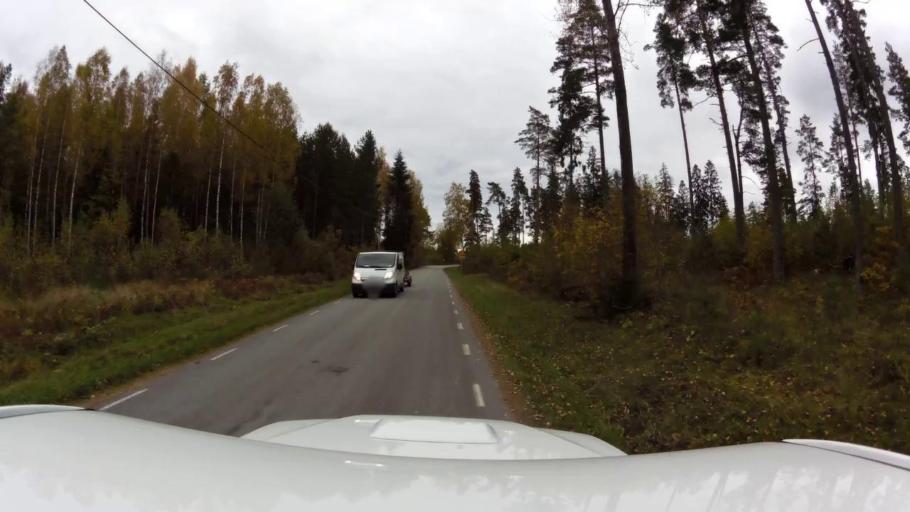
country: SE
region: OEstergoetland
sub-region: Linkopings Kommun
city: Ljungsbro
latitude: 58.5243
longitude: 15.4873
